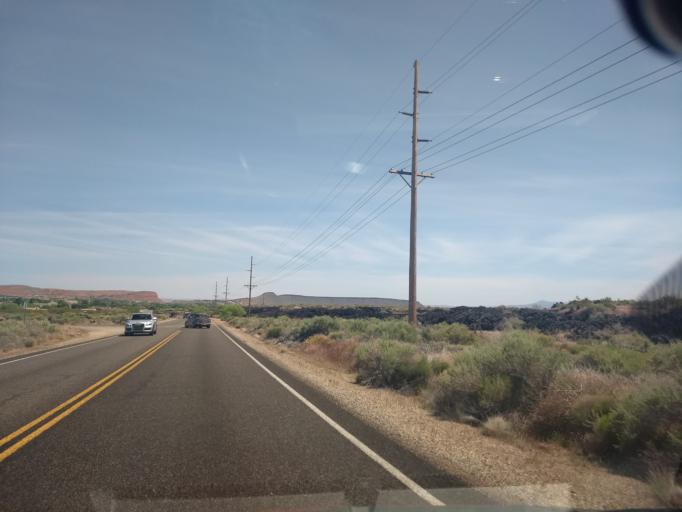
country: US
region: Utah
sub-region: Washington County
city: Santa Clara
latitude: 37.1428
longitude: -113.6446
